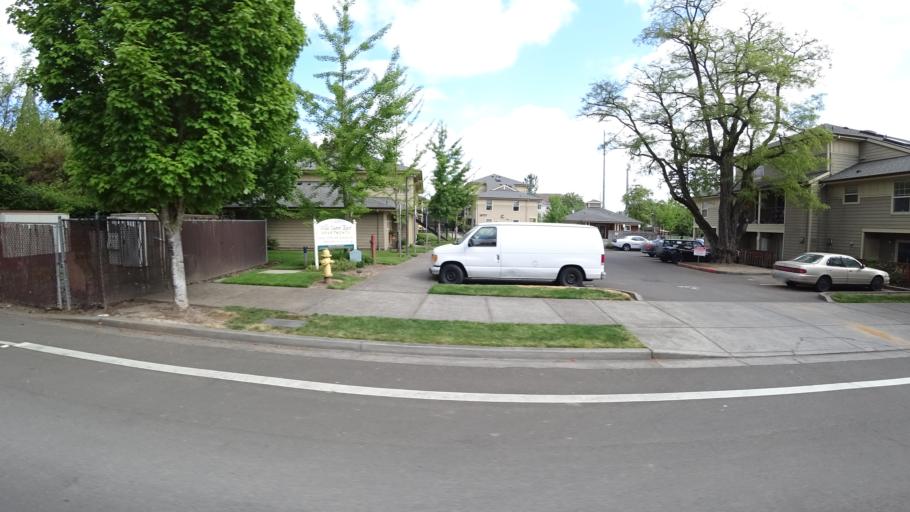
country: US
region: Oregon
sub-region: Washington County
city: Rockcreek
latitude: 45.5231
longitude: -122.8914
